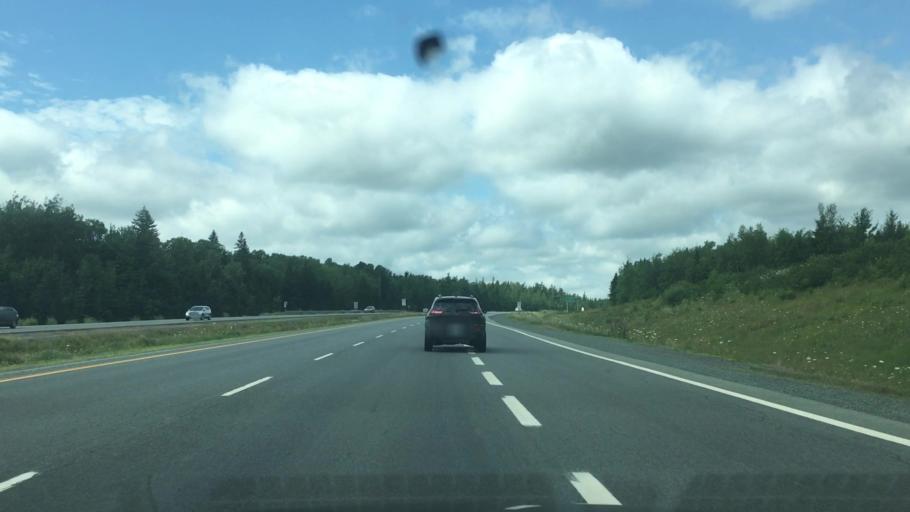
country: CA
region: Nova Scotia
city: Springhill
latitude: 45.6923
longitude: -64.0095
